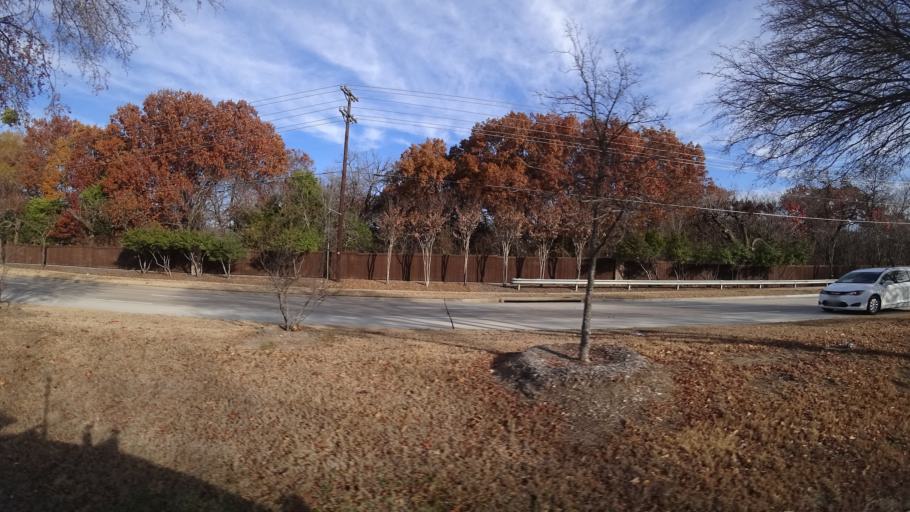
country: US
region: Texas
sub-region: Collin County
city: Fairview
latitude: 33.1969
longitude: -96.6766
